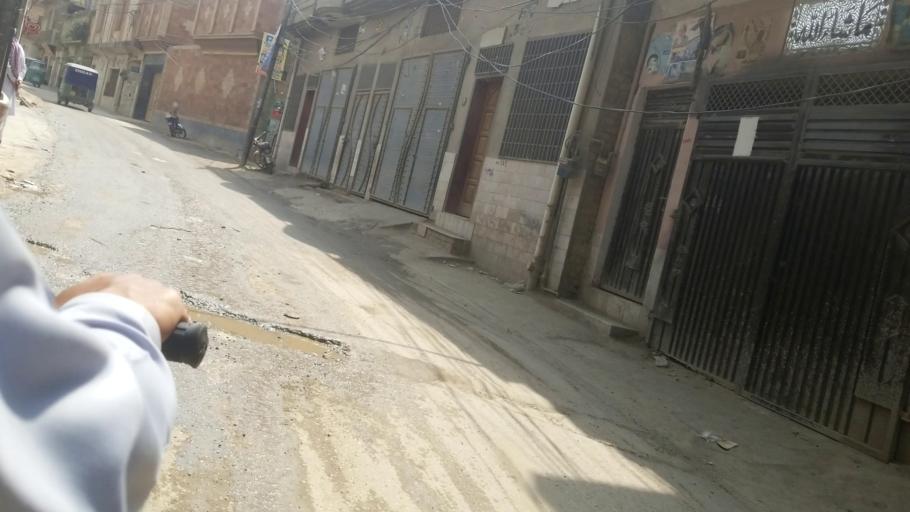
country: PK
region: Khyber Pakhtunkhwa
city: Peshawar
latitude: 33.9836
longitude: 71.5358
